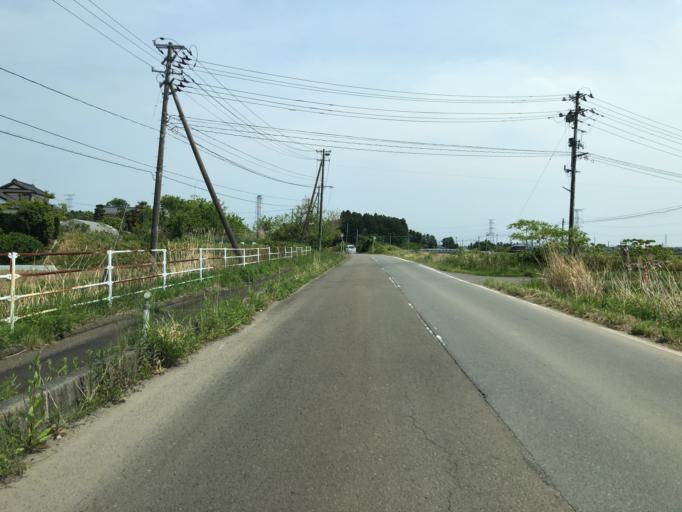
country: JP
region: Miyagi
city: Marumori
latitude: 37.8471
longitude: 140.9223
